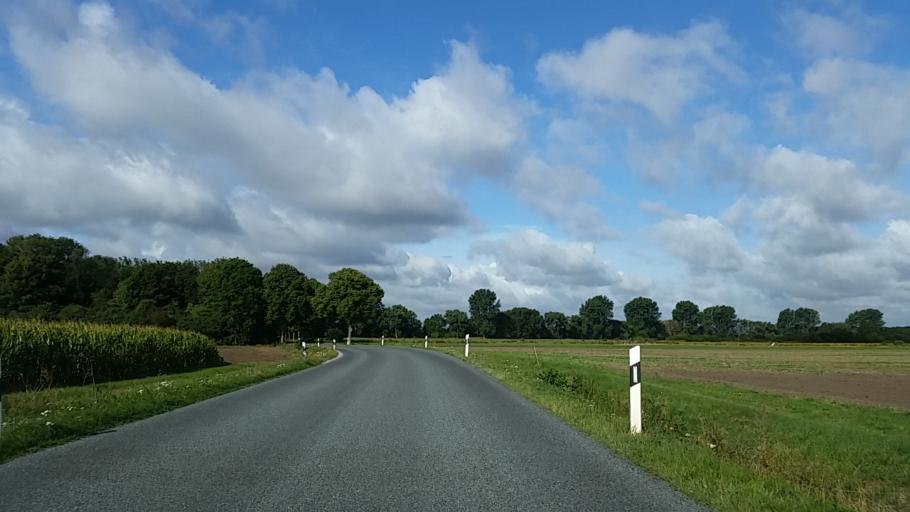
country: DE
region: Lower Saxony
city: Sickte
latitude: 52.2023
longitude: 10.6088
